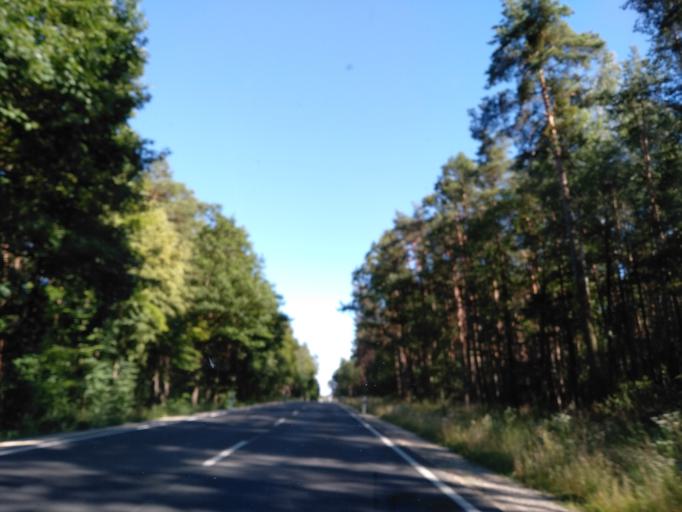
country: DE
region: Bavaria
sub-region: Regierungsbezirk Mittelfranken
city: Hessdorf
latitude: 49.6413
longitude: 10.9258
